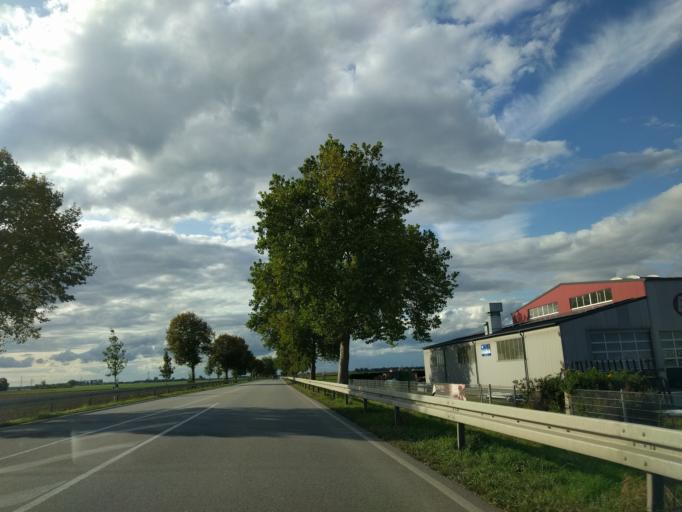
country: DE
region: Bavaria
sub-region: Lower Bavaria
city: Stephansposching
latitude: 48.8015
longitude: 12.8017
